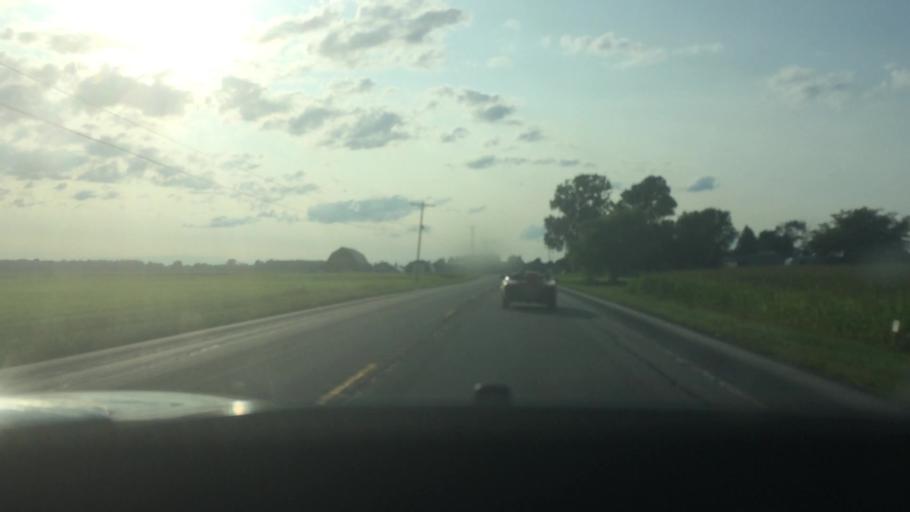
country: US
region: New York
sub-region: St. Lawrence County
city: Ogdensburg
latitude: 44.6618
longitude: -75.3390
